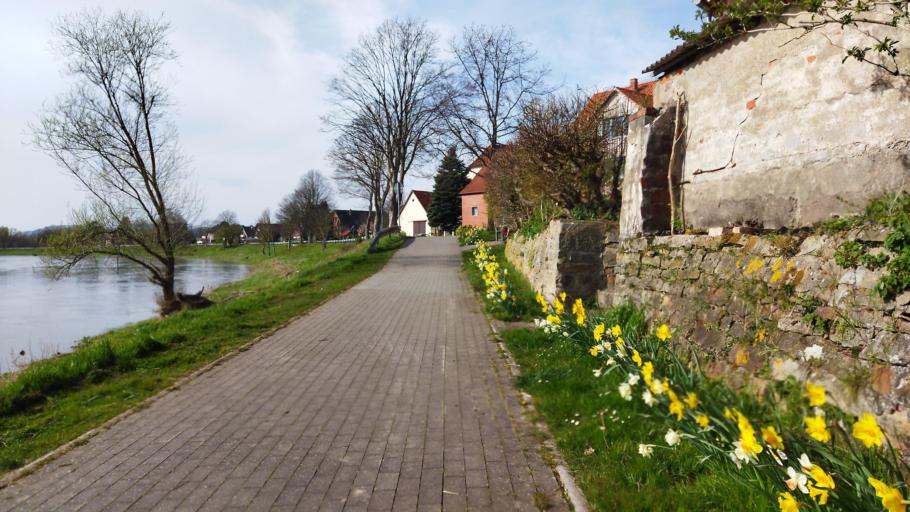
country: DE
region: Lower Saxony
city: Hessisch Oldendorf
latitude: 52.1748
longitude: 9.1878
